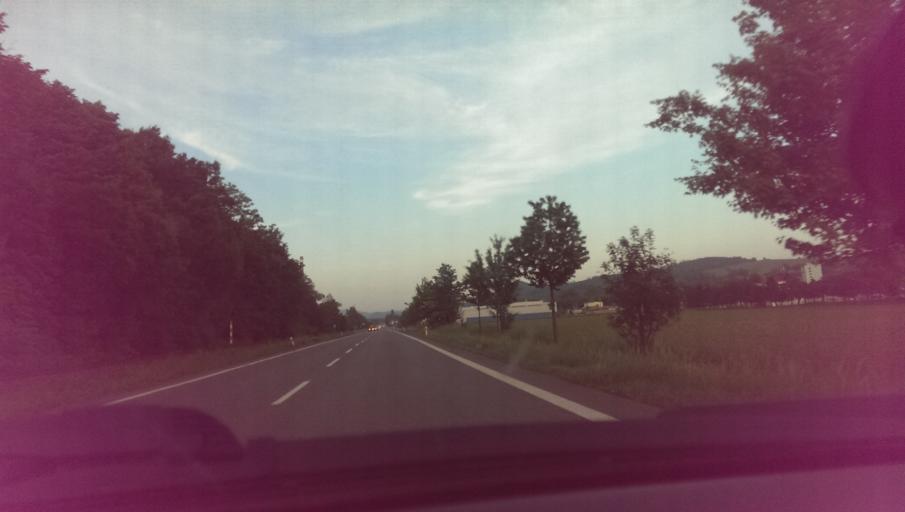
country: CZ
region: Zlin
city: Zubri
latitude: 49.4621
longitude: 18.0765
